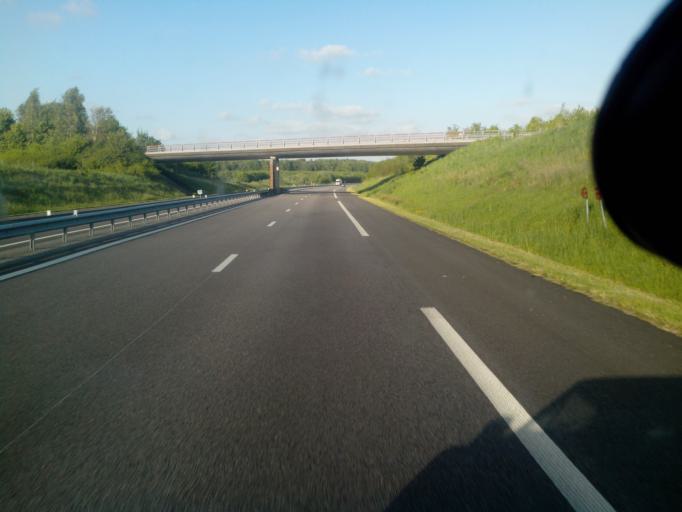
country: FR
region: Haute-Normandie
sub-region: Departement de la Seine-Maritime
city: Bosc-le-Hard
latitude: 49.6384
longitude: 1.1893
